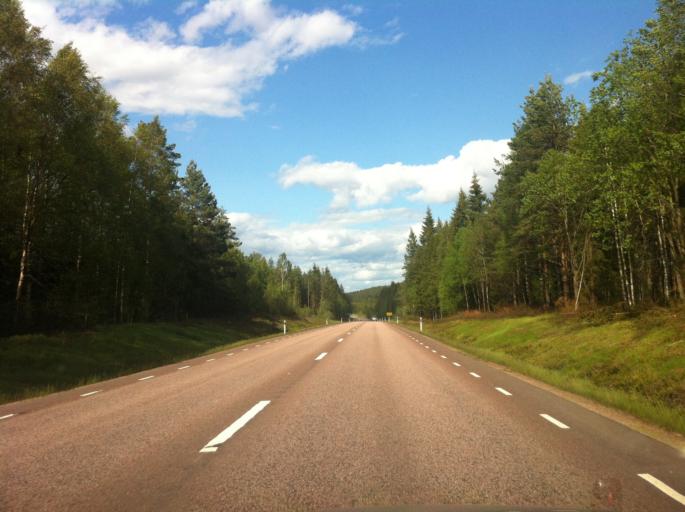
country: SE
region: Vaermland
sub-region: Kristinehamns Kommun
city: Kristinehamn
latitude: 59.3581
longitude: 14.1491
